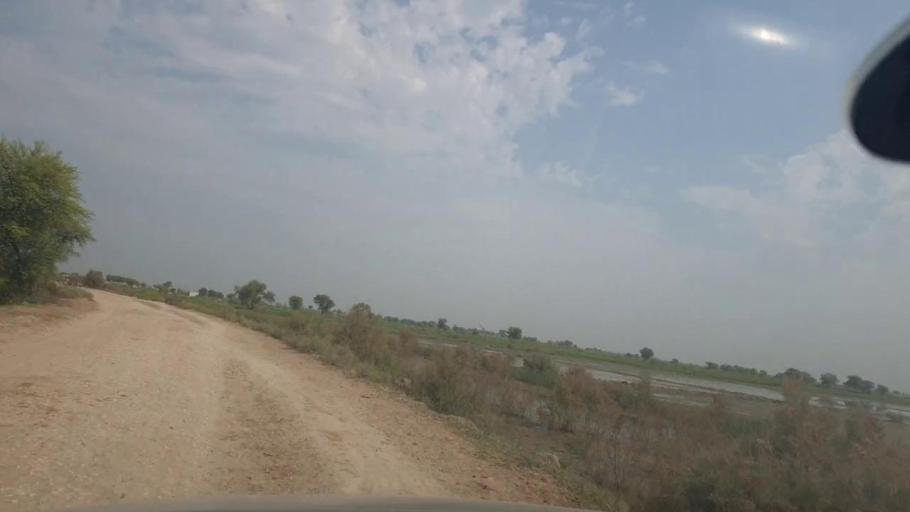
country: PK
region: Balochistan
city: Mehrabpur
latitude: 28.1233
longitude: 68.0906
